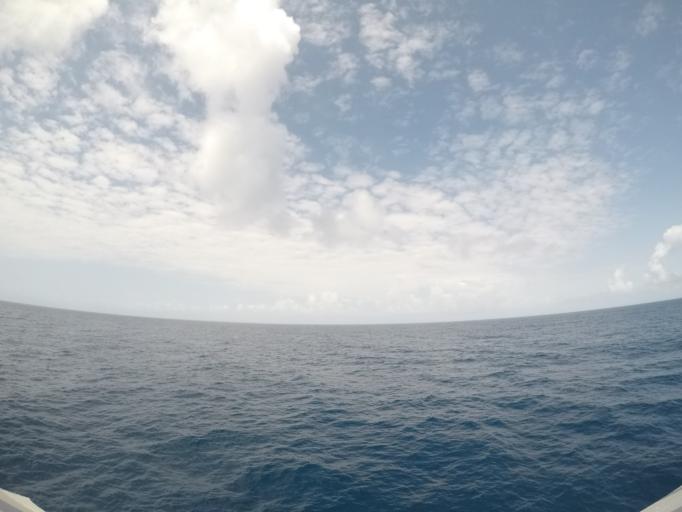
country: TZ
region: Zanzibar North
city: Nungwi
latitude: -5.5725
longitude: 39.3666
